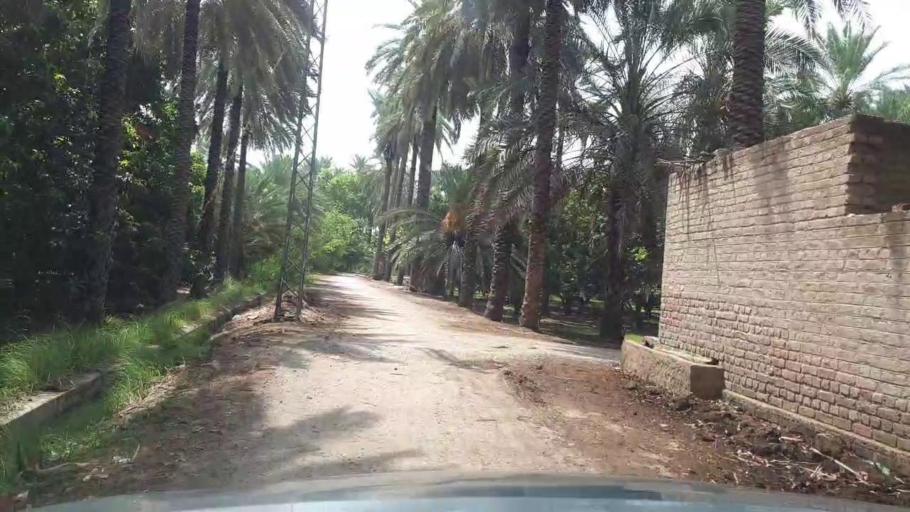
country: PK
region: Sindh
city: Pir jo Goth
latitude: 27.6175
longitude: 68.6756
